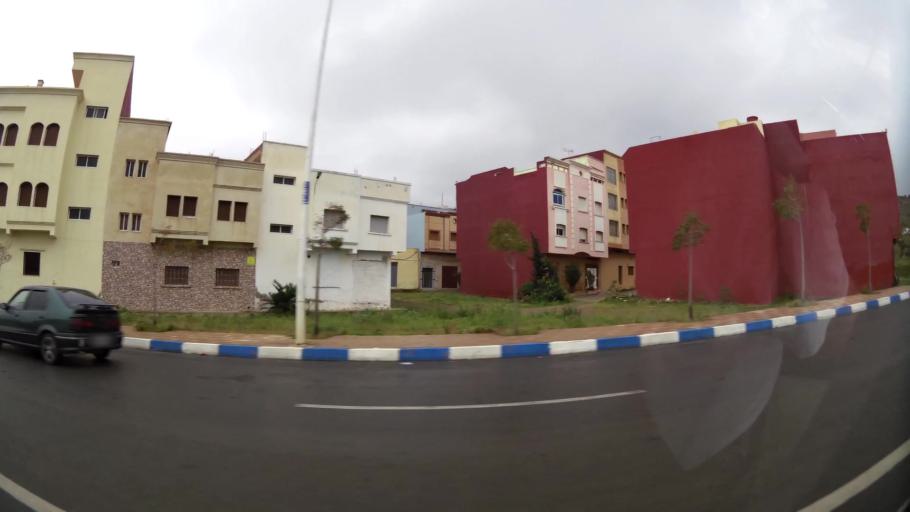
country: MA
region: Oriental
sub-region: Nador
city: Nador
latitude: 35.1906
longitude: -2.9298
